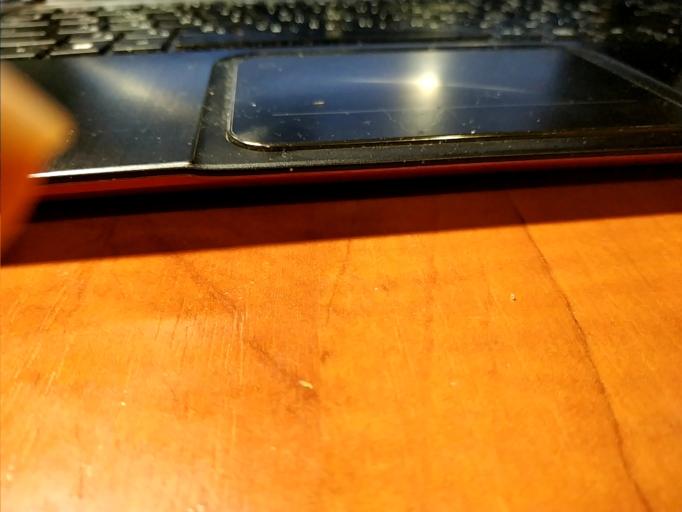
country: RU
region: Republic of Karelia
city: Kem'
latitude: 64.6900
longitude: 33.9890
